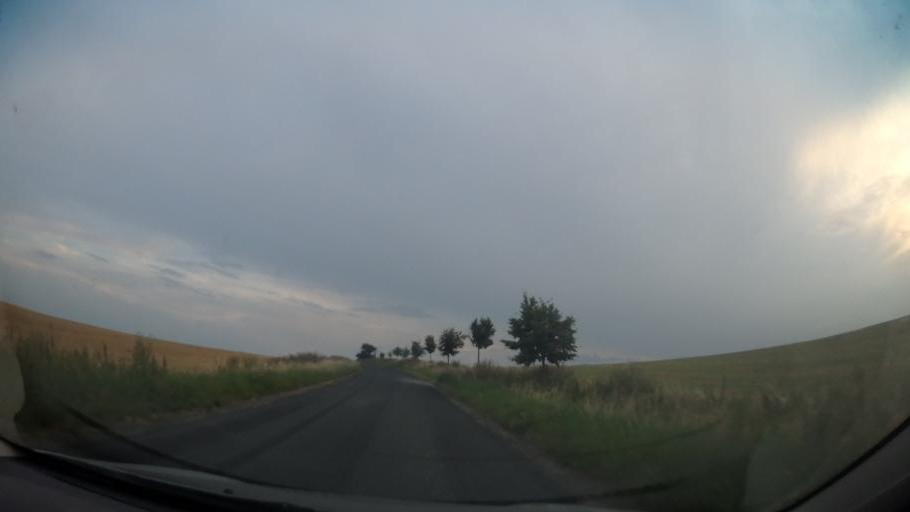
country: CZ
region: South Moravian
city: Orechov
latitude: 49.0886
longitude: 16.4963
